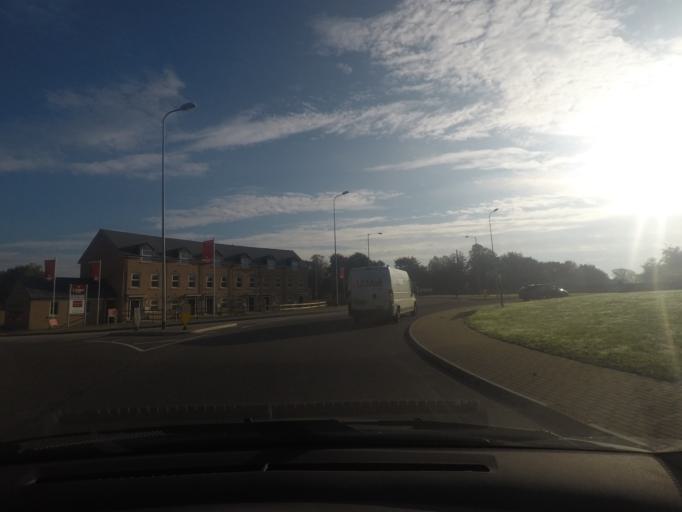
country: GB
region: England
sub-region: East Riding of Yorkshire
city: Market Weighton
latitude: 53.8616
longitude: -0.6814
